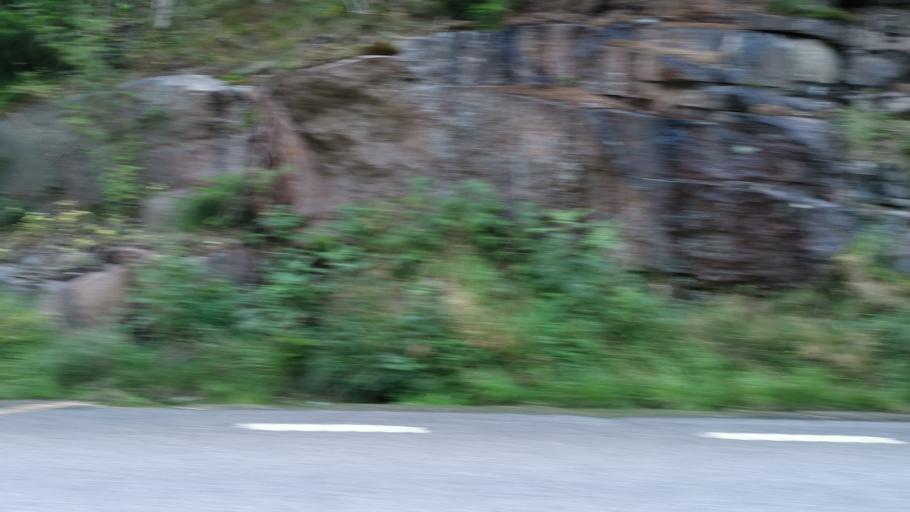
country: SE
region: Vaestra Goetaland
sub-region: Lysekils Kommun
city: Brastad
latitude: 58.4559
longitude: 11.4896
